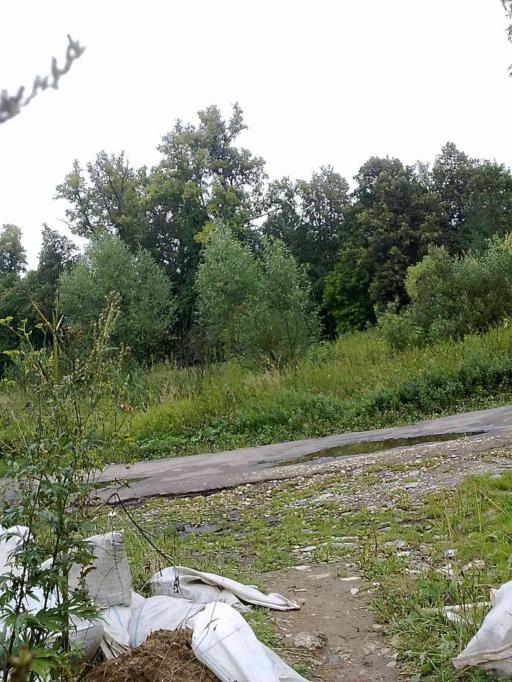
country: RU
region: Moskovskaya
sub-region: Leninskiy Rayon
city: Vnukovo
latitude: 55.6278
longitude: 37.2631
